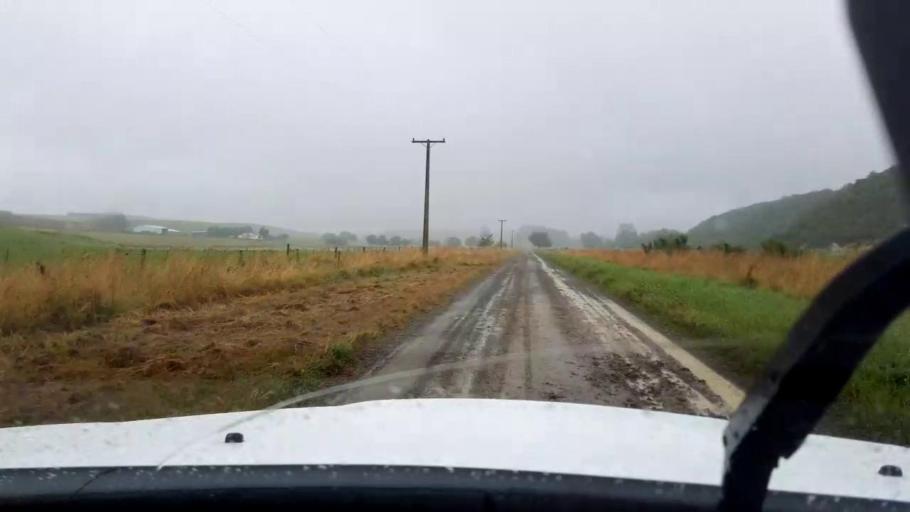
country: NZ
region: Canterbury
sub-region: Timaru District
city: Pleasant Point
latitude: -44.1666
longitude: 171.1880
